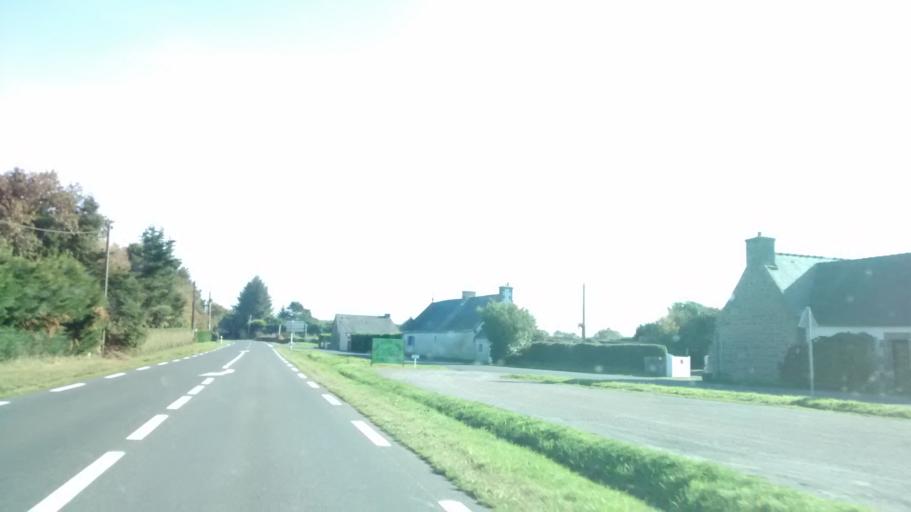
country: FR
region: Brittany
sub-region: Departement des Cotes-d'Armor
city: Pleumeur-Bodou
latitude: 48.7540
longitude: -3.5205
